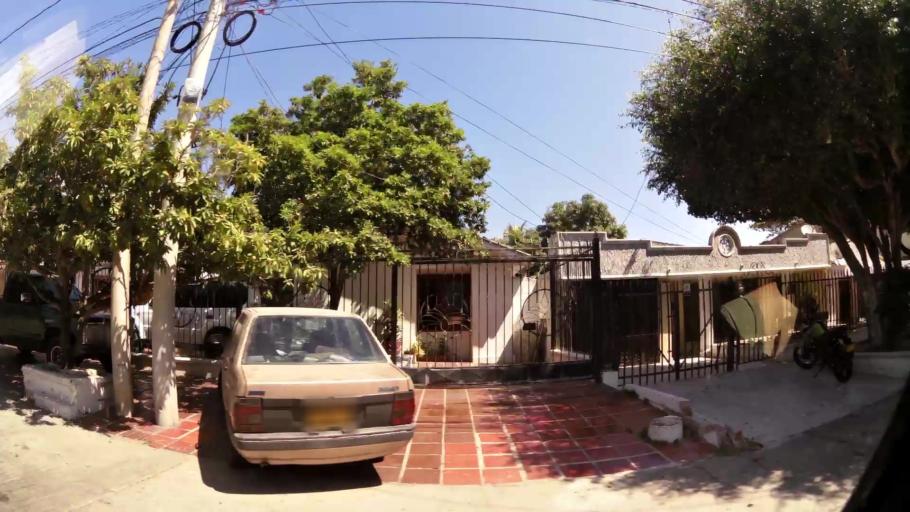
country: CO
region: Atlantico
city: Barranquilla
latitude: 11.0070
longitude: -74.7963
